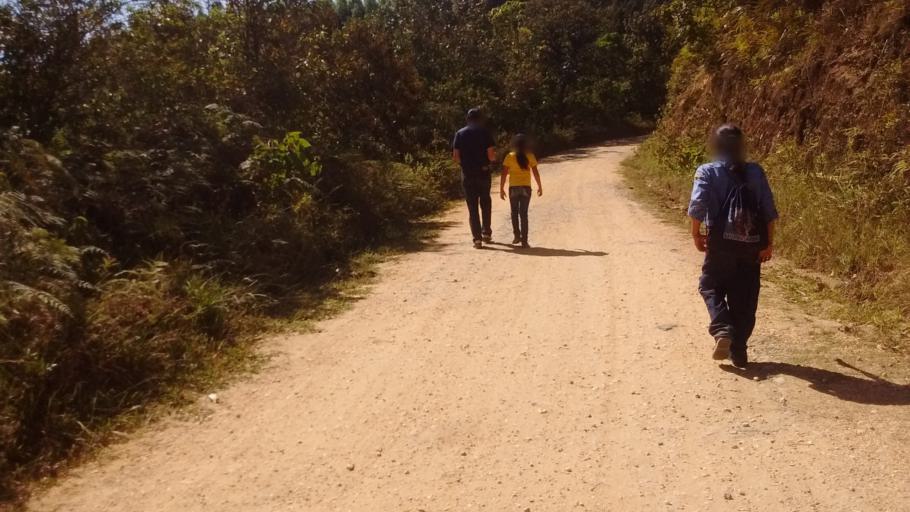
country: CO
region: Cauca
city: Popayan
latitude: 2.4604
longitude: -76.5711
